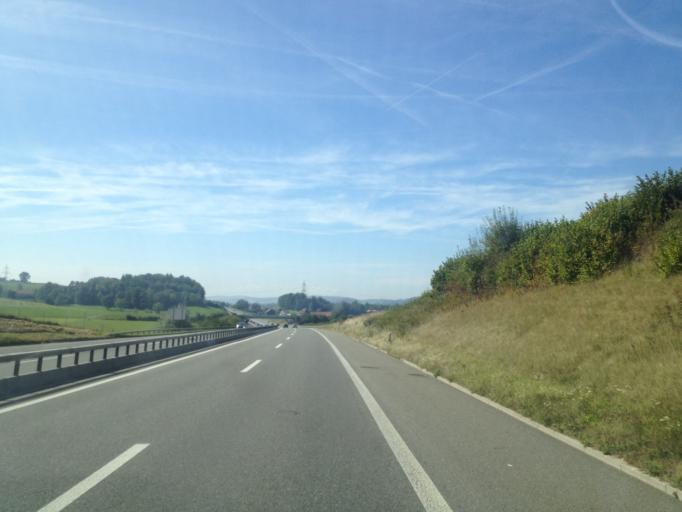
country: CH
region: Fribourg
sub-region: Sense District
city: Bosingen
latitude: 46.8690
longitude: 7.2206
